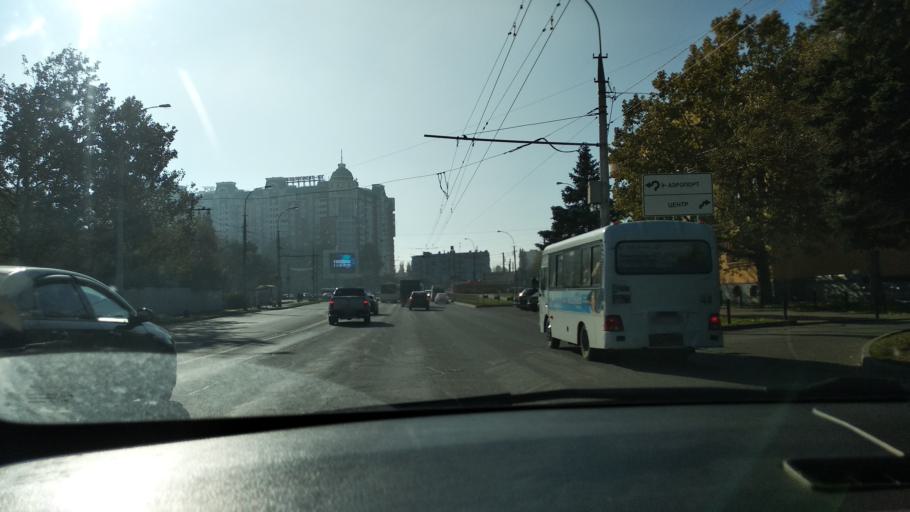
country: RU
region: Krasnodarskiy
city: Pashkovskiy
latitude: 45.0168
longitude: 39.0478
